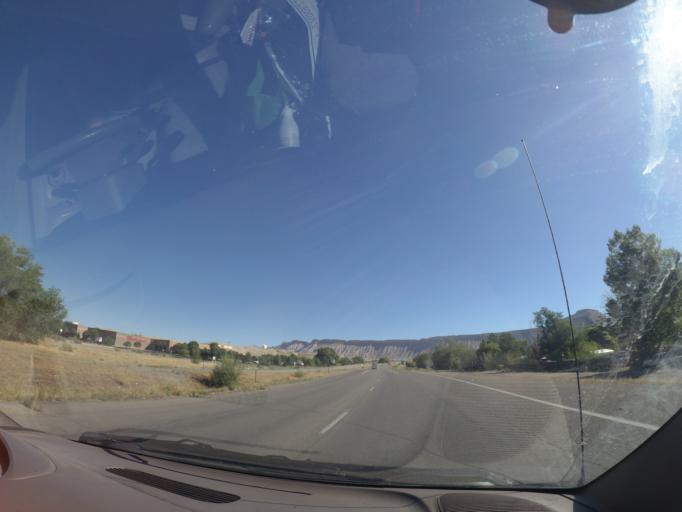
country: US
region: Colorado
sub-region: Mesa County
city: Clifton
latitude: 39.0961
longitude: -108.4487
